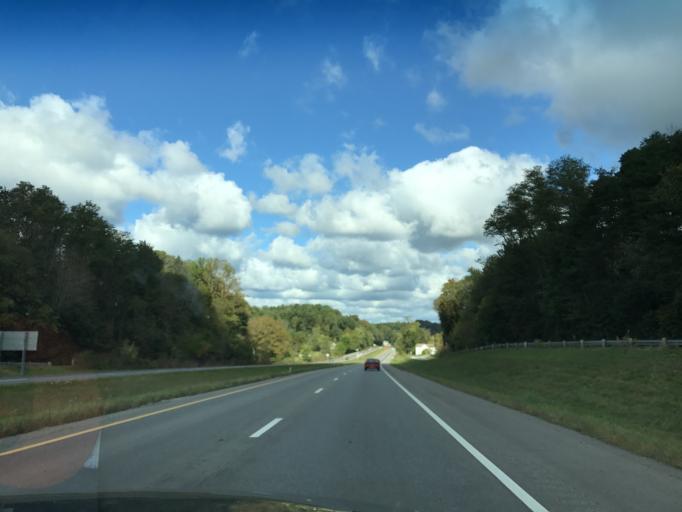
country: US
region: Ohio
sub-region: Hocking County
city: Logan
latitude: 39.5676
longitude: -82.5137
